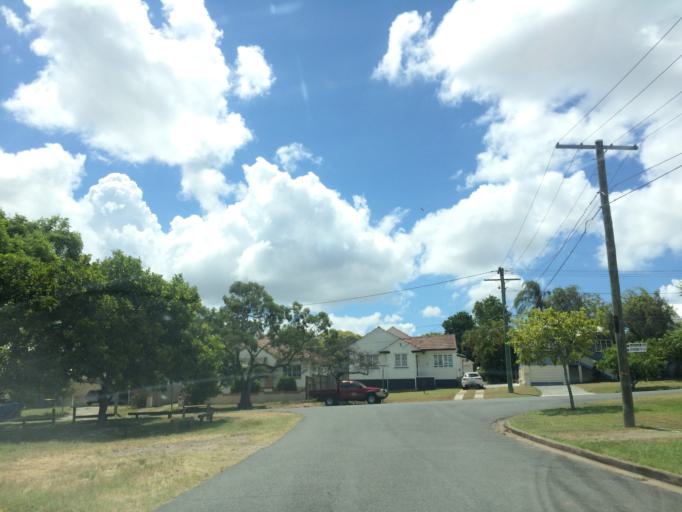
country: AU
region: Queensland
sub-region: Brisbane
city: Seven Hills
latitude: -27.4881
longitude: 153.0601
